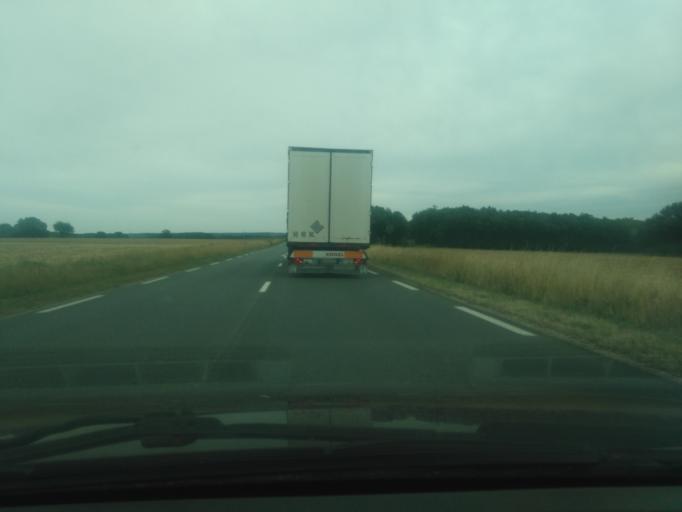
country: FR
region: Poitou-Charentes
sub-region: Departement de la Vienne
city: Bonnes
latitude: 46.5647
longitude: 0.5868
